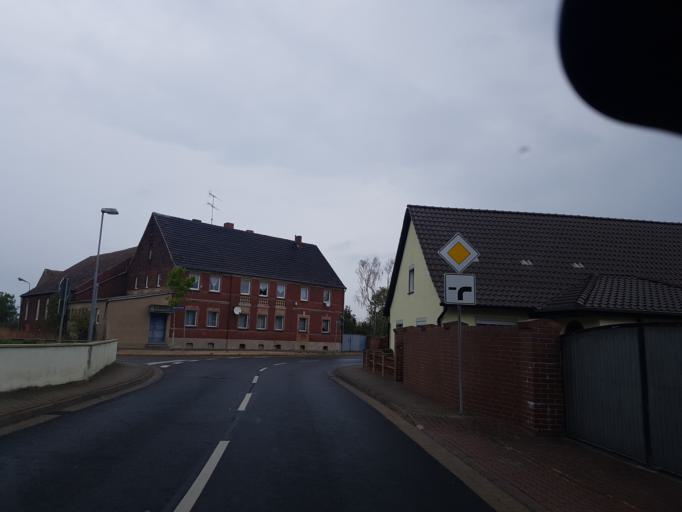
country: DE
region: Saxony-Anhalt
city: Jessen
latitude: 51.7674
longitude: 12.9071
